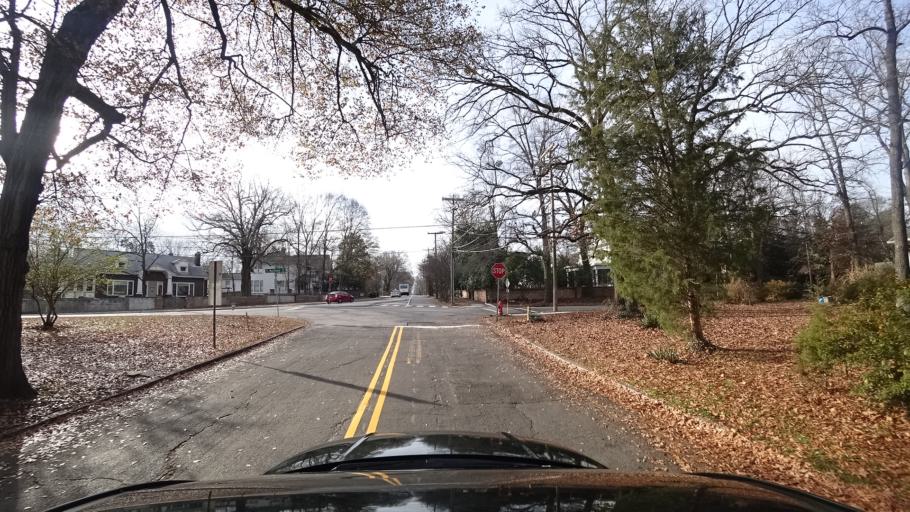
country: US
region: North Carolina
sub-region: Durham County
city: Durham
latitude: 36.0100
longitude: -78.8930
